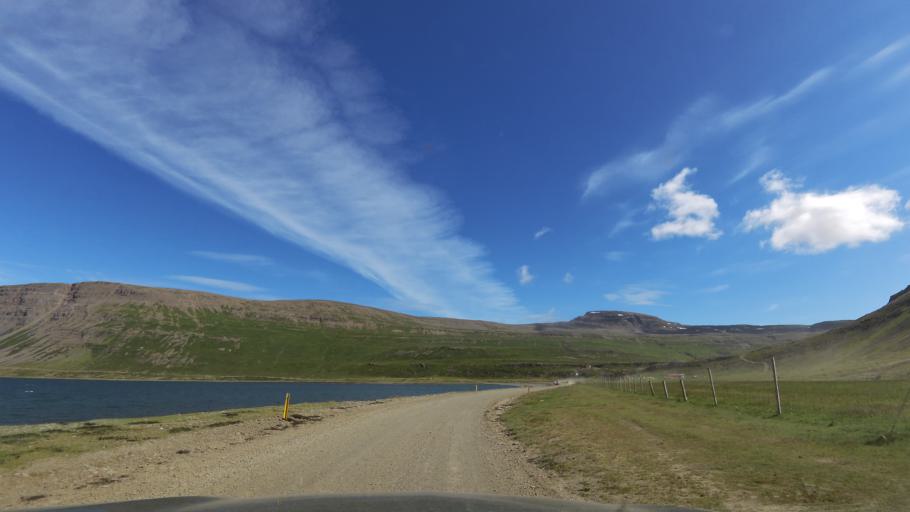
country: IS
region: Westfjords
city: Isafjoerdur
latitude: 65.6061
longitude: -23.5595
